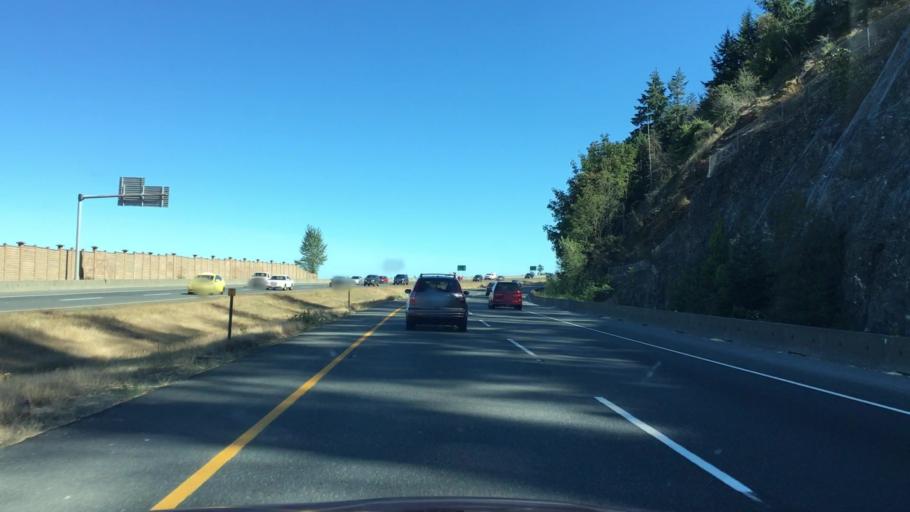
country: CA
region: British Columbia
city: Nanaimo
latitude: 49.1633
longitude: -123.9751
